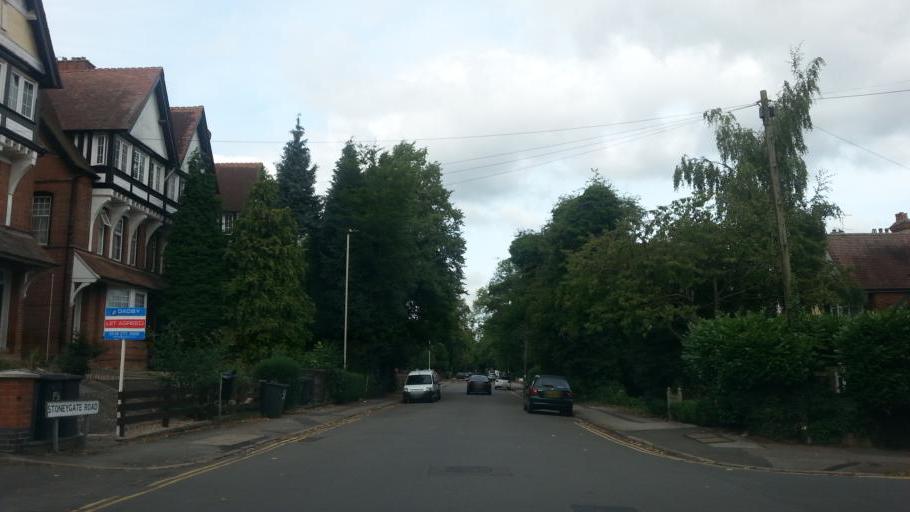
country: GB
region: England
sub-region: Leicestershire
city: Oadby
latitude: 52.6165
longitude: -1.1030
